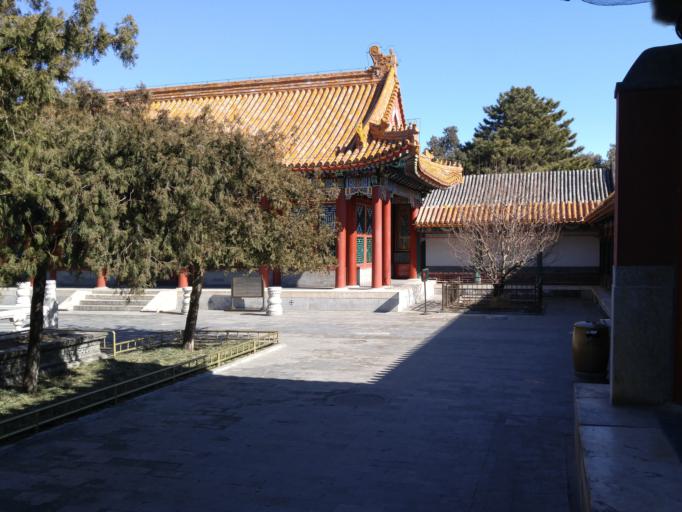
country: CN
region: Beijing
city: Haidian
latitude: 39.9967
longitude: 116.2681
